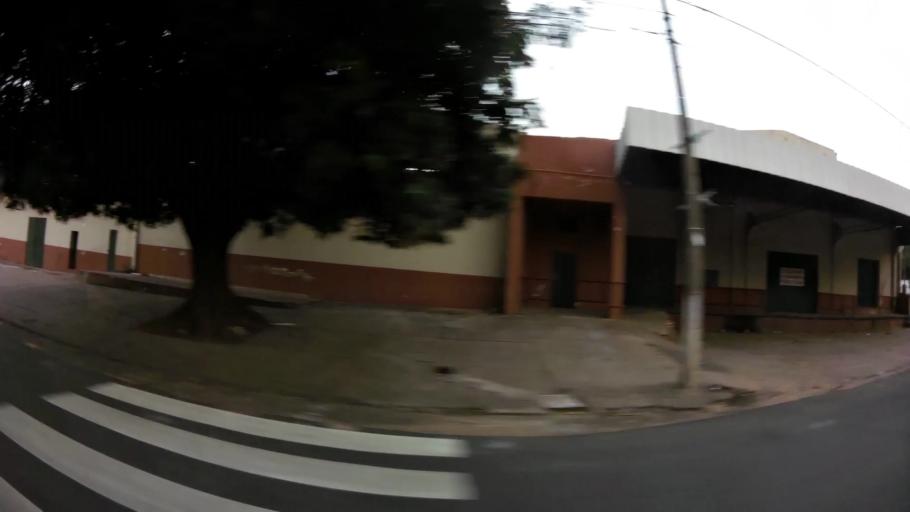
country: PY
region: Asuncion
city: Asuncion
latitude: -25.3130
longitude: -57.6178
